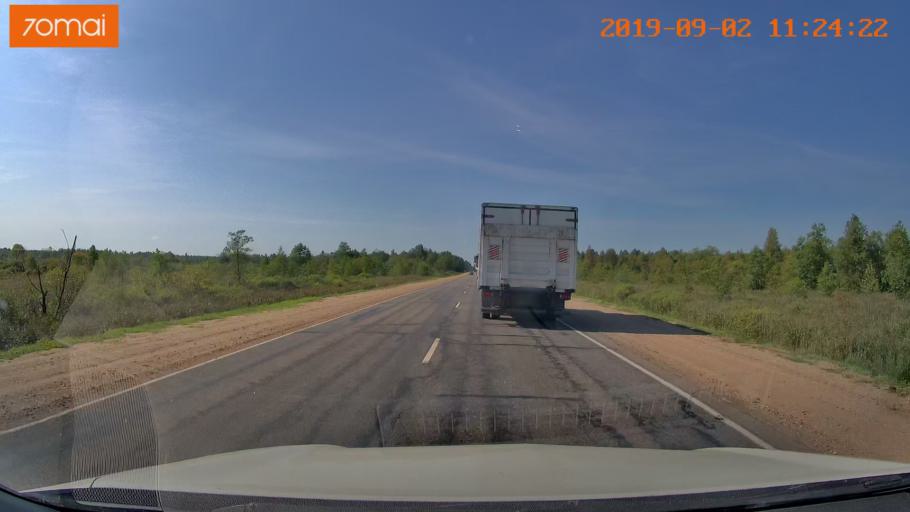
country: RU
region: Smolensk
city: Roslavl'
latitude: 54.0109
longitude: 32.9765
